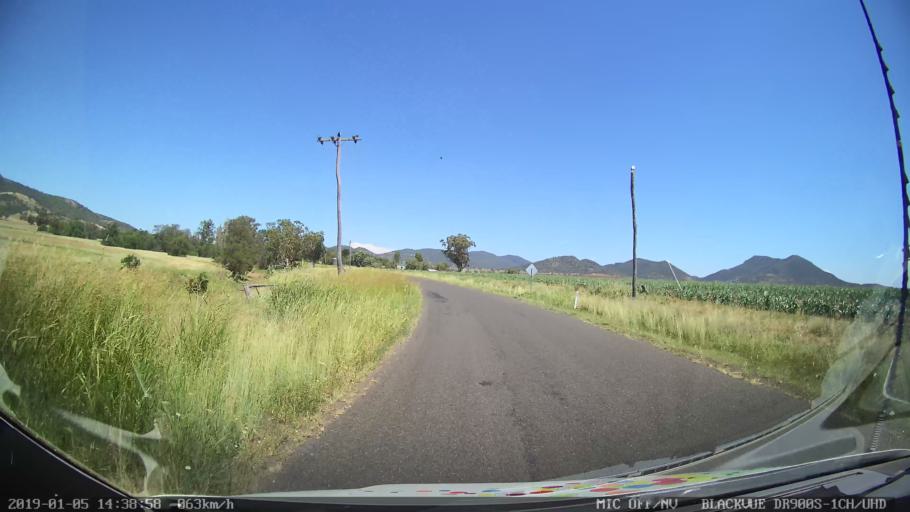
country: AU
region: New South Wales
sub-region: Tamworth Municipality
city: Phillip
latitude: -31.2526
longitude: 150.6953
